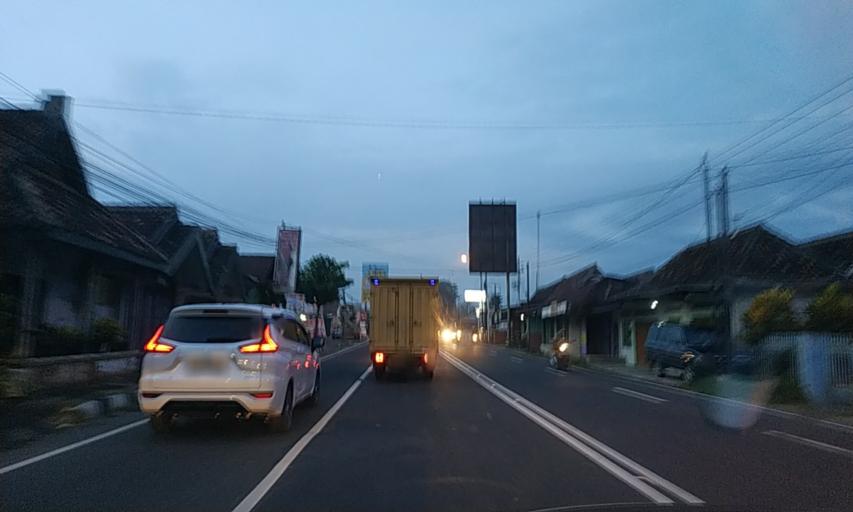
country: ID
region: Daerah Istimewa Yogyakarta
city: Godean
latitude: -7.8351
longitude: 110.2202
